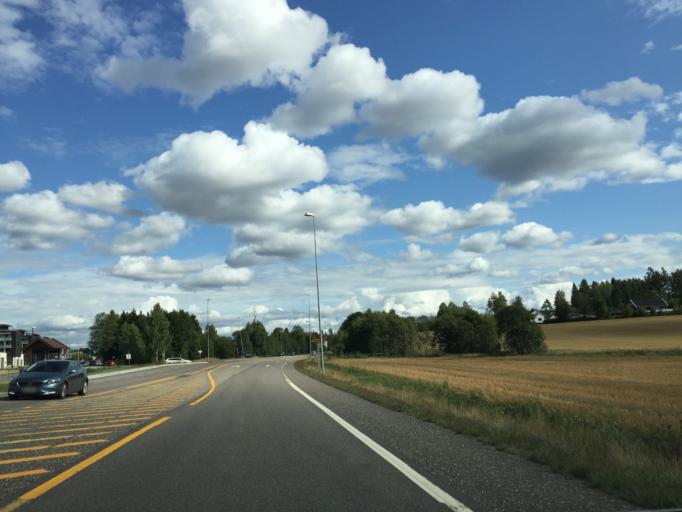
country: NO
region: Ostfold
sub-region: Hobol
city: Knappstad
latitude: 59.6201
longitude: 11.0212
